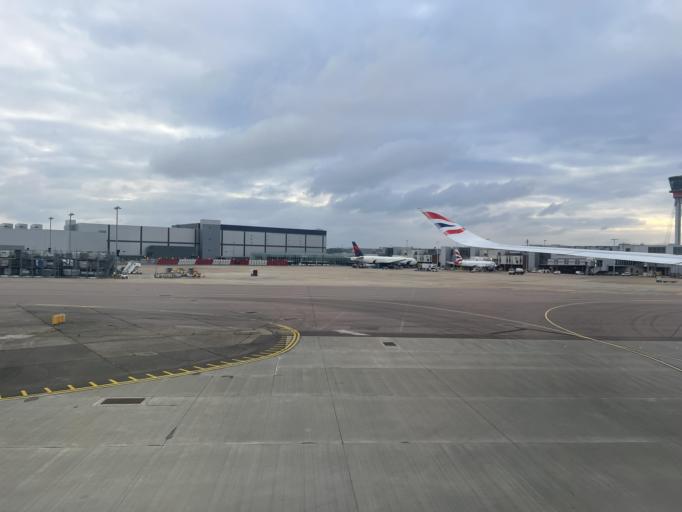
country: GB
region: England
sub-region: Greater London
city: West Drayton
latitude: 51.4759
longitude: -0.4604
